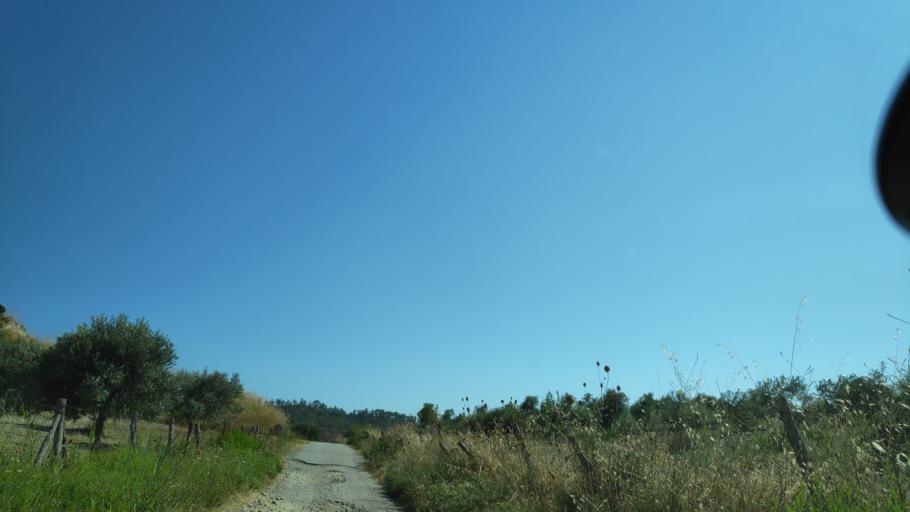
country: IT
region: Calabria
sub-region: Provincia di Reggio Calabria
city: Monasterace
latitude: 38.4327
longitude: 16.5249
